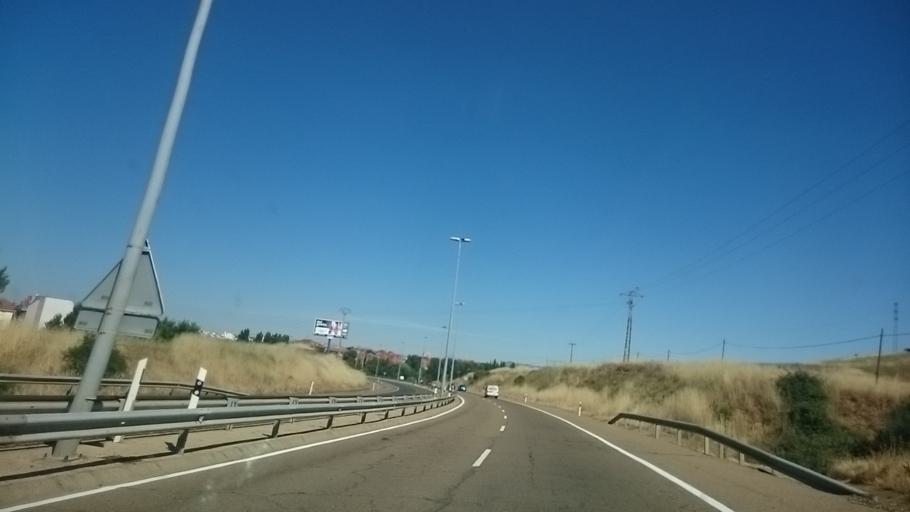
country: ES
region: Castille and Leon
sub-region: Provincia de Leon
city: Leon
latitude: 42.5835
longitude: -5.5479
